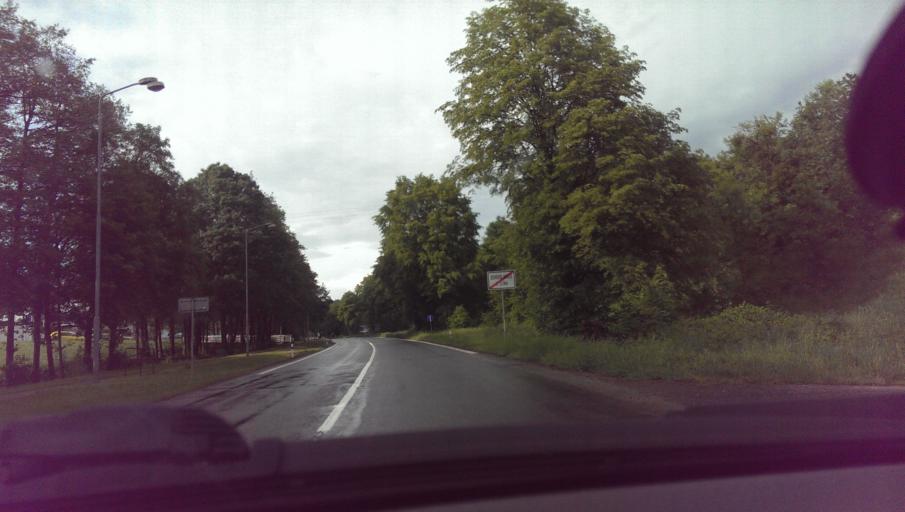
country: CZ
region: Zlin
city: Breznice
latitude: 49.1702
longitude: 17.6404
